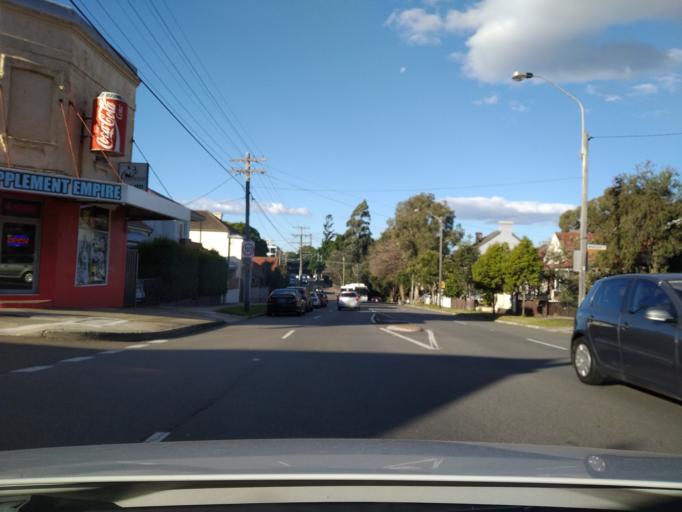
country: AU
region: New South Wales
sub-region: Ashfield
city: Summer Hill
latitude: -33.8955
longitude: 151.1406
